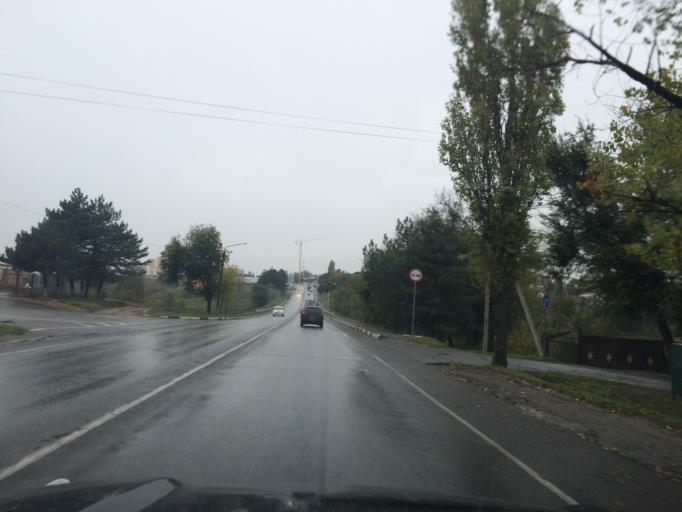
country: RU
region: Rostov
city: Azov
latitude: 47.0890
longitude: 39.4599
